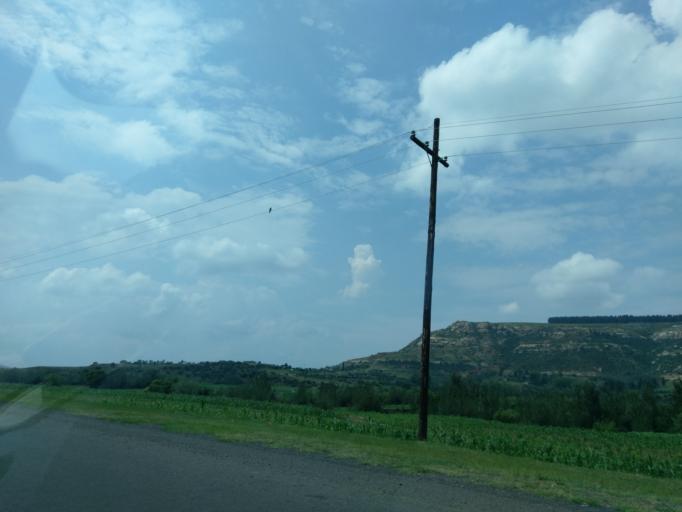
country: LS
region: Leribe
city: Leribe
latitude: -29.0081
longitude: 27.9975
